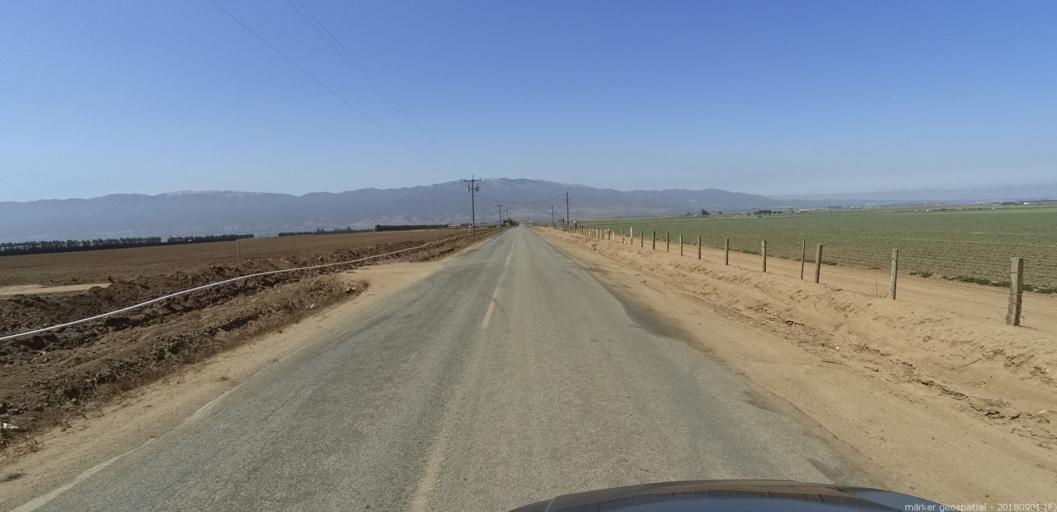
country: US
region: California
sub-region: Monterey County
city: Chualar
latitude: 36.5860
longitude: -121.4694
